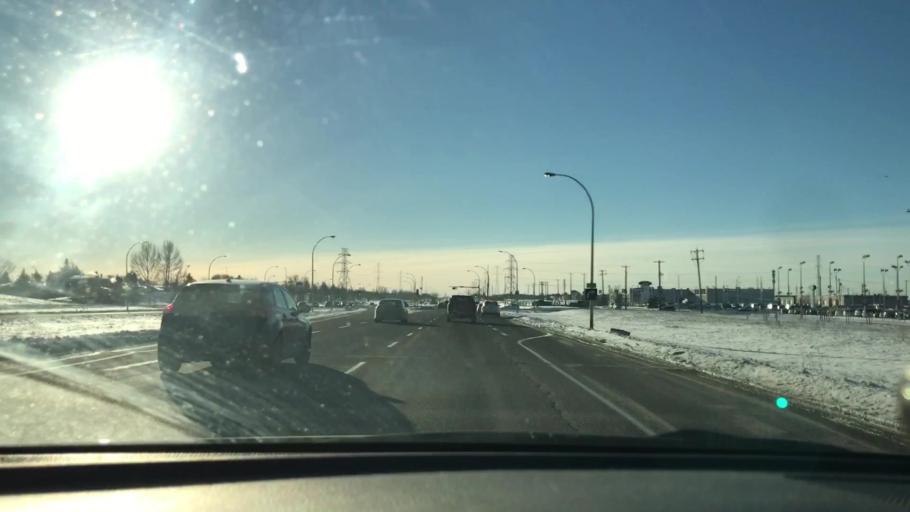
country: CA
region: Alberta
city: Edmonton
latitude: 53.4673
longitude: -113.4669
